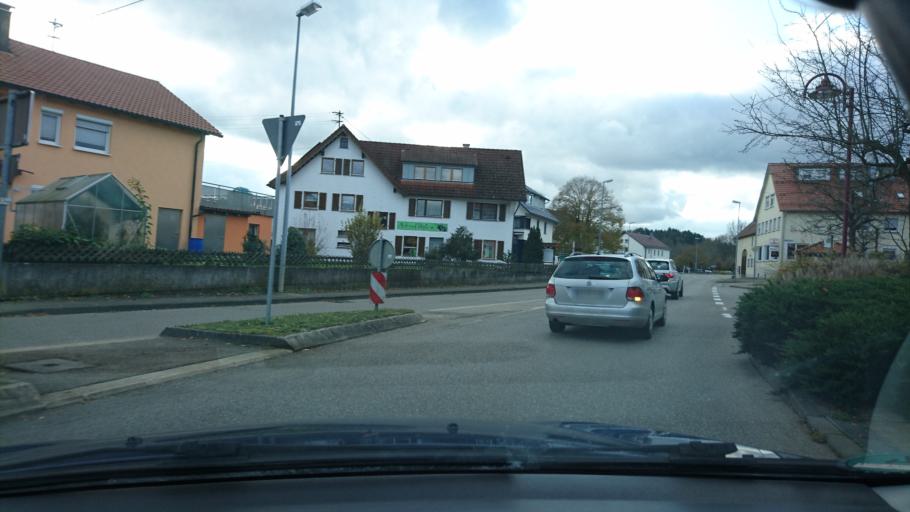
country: DE
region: Baden-Wuerttemberg
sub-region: Regierungsbezirk Stuttgart
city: Heuchlingen
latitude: 48.8528
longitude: 9.9433
